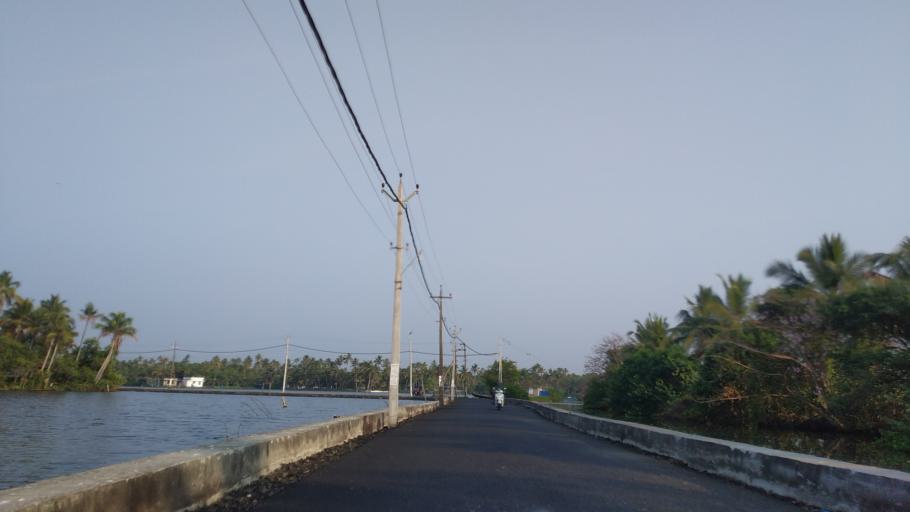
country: IN
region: Kerala
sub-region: Ernakulam
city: Elur
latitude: 10.1069
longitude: 76.1928
